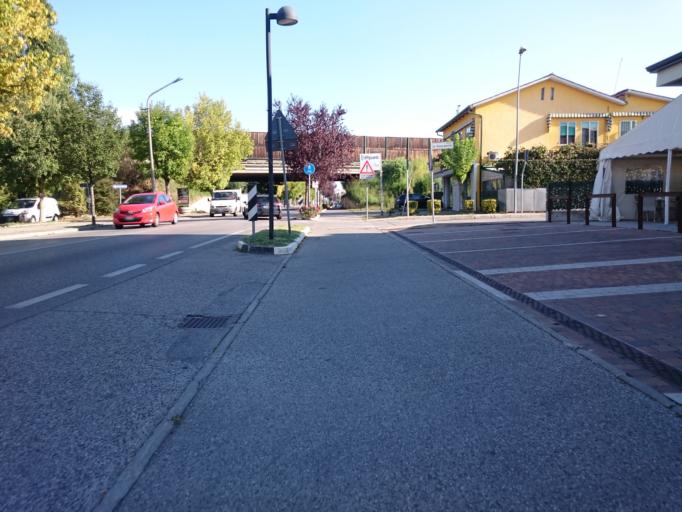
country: IT
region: Veneto
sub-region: Provincia di Padova
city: Masera di Padova
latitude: 45.3392
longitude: 11.8663
